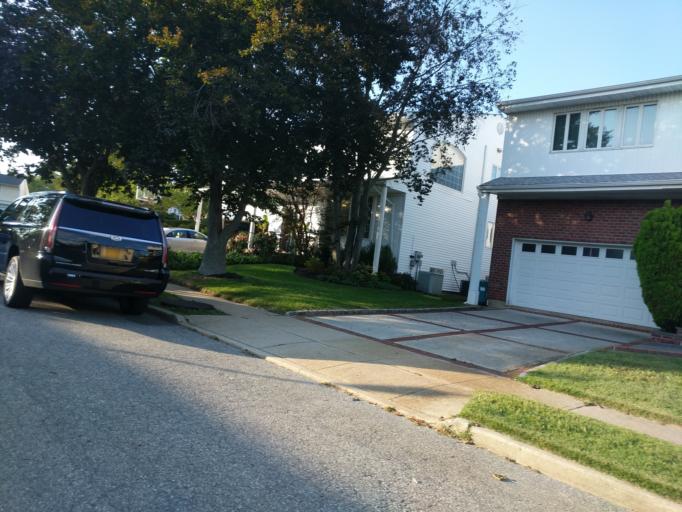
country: US
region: New York
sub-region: Nassau County
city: South Valley Stream
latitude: 40.6422
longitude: -73.7346
